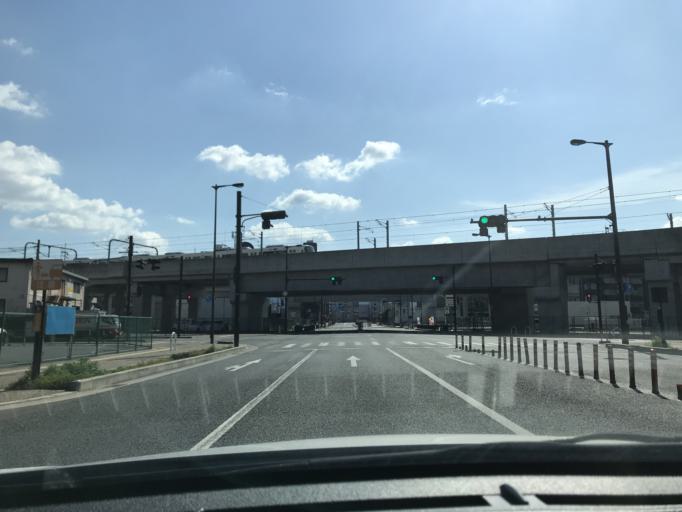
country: JP
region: Nara
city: Nara-shi
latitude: 34.6774
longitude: 135.8162
